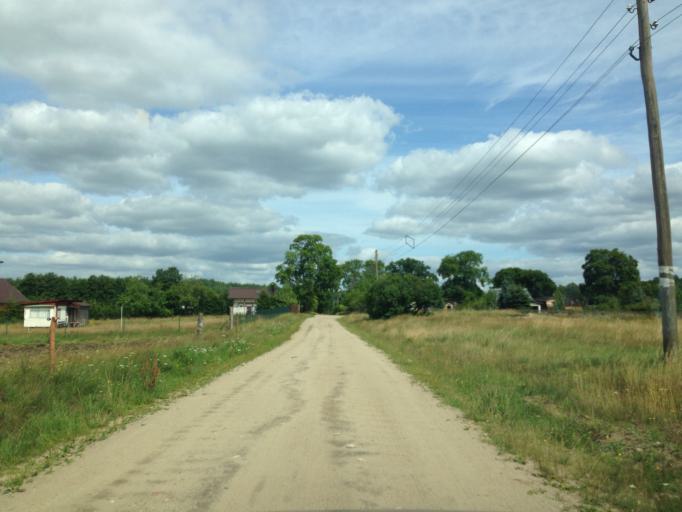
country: PL
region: Pomeranian Voivodeship
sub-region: Powiat bytowski
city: Studzienice
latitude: 54.0721
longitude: 17.6799
